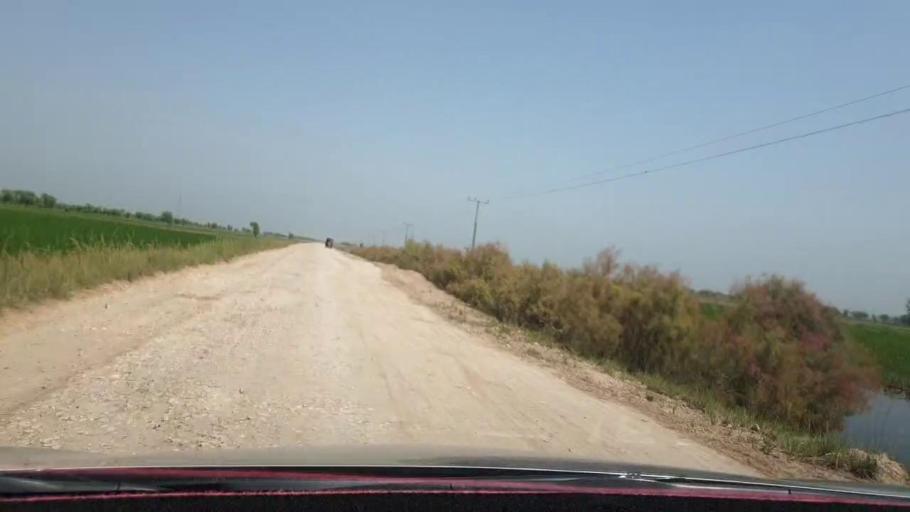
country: PK
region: Sindh
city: Warah
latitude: 27.4354
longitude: 67.7257
